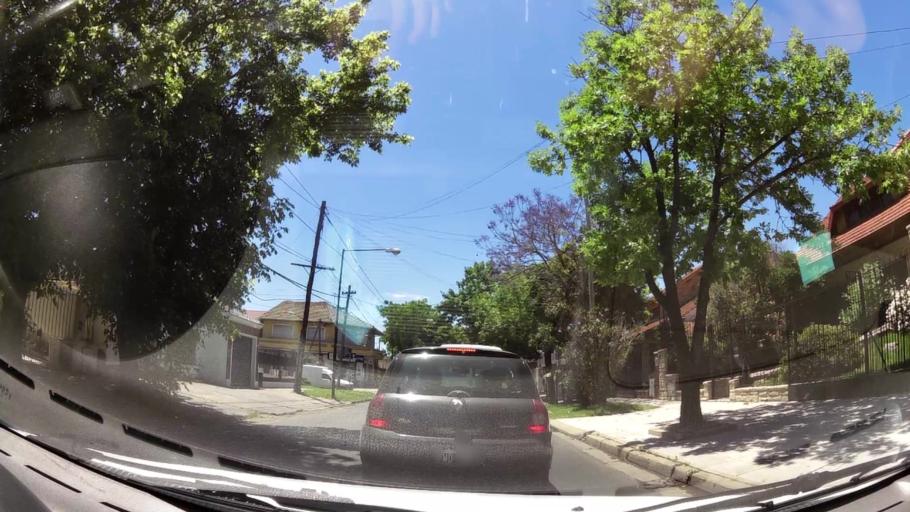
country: AR
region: Buenos Aires
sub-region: Partido de Vicente Lopez
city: Olivos
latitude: -34.5020
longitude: -58.5188
